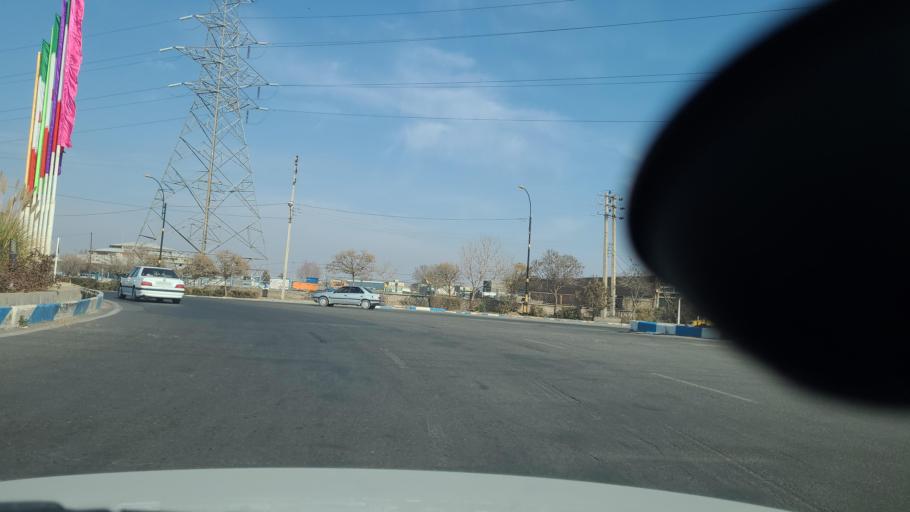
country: IR
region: Razavi Khorasan
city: Fariman
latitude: 35.7063
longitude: 59.8367
